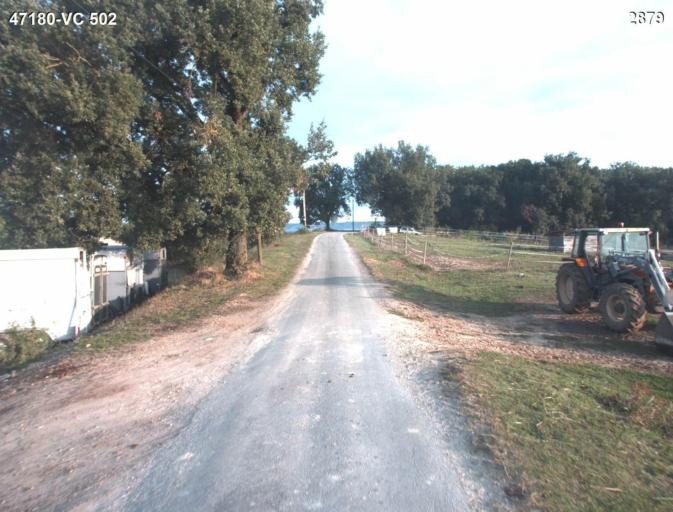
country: FR
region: Aquitaine
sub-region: Departement du Lot-et-Garonne
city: Sainte-Colombe-en-Bruilhois
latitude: 44.1824
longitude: 0.4826
